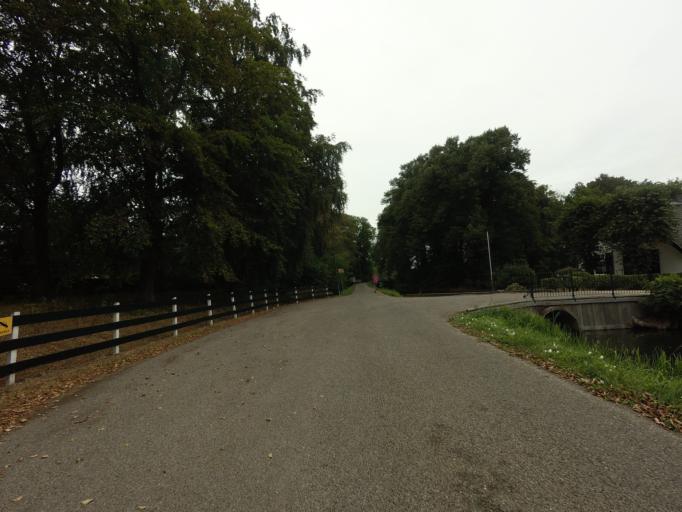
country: NL
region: Utrecht
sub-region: Stichtse Vecht
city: Maarssen
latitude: 52.1273
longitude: 5.0752
